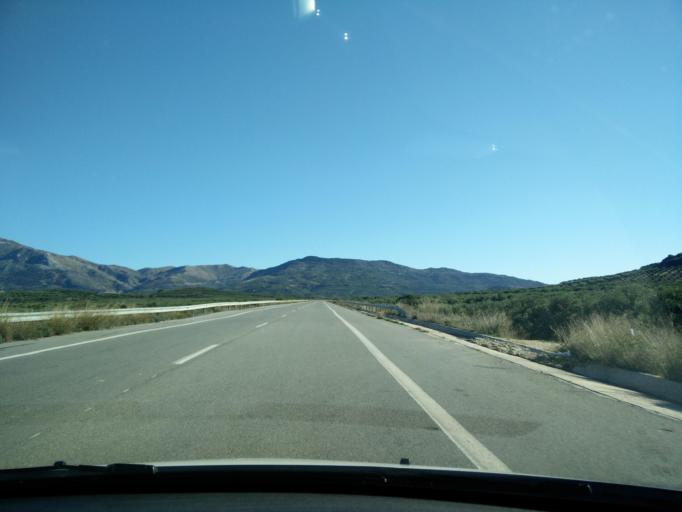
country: GR
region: Crete
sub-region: Nomos Irakleiou
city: Arkalochori
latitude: 35.0886
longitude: 25.3076
